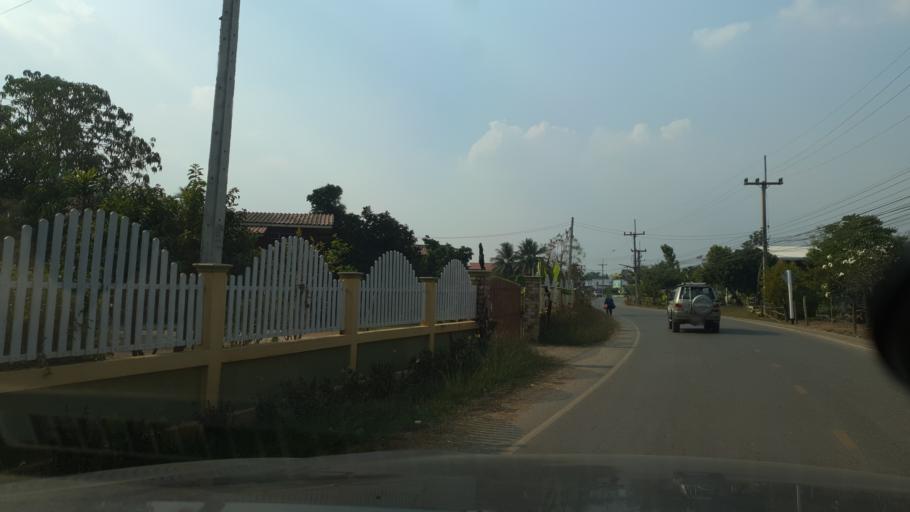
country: TH
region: Sukhothai
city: Ban Dan Lan Hoi
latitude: 17.1133
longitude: 99.5483
